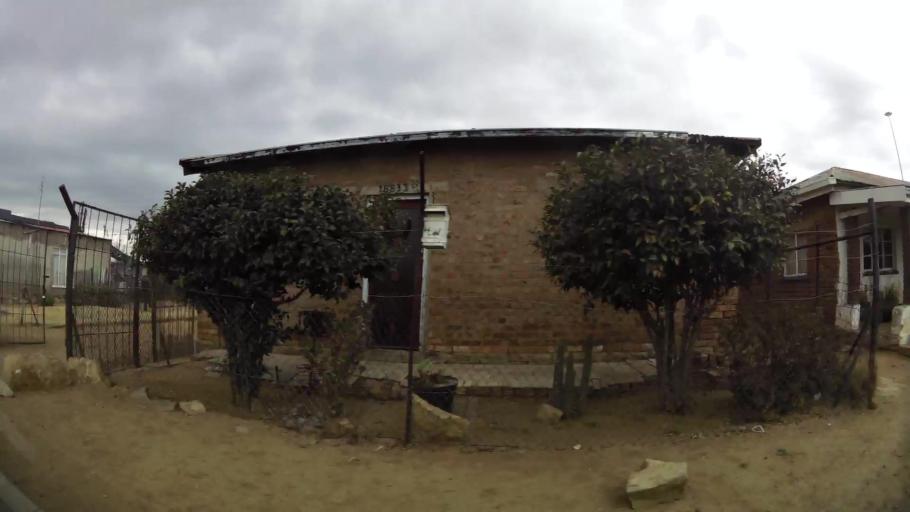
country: ZA
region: Orange Free State
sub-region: Fezile Dabi District Municipality
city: Kroonstad
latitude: -27.6469
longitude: 27.2169
